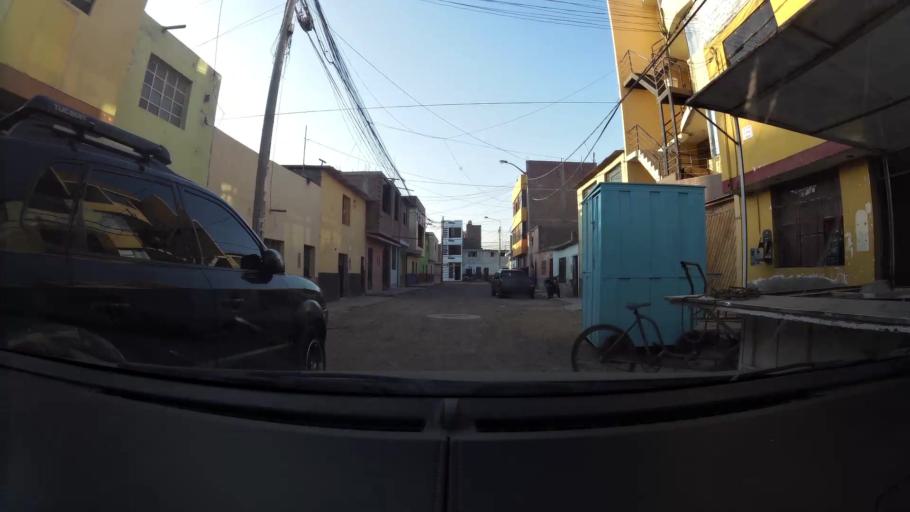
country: PE
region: Lambayeque
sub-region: Provincia de Chiclayo
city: Santa Rosa
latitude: -6.7689
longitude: -79.8292
